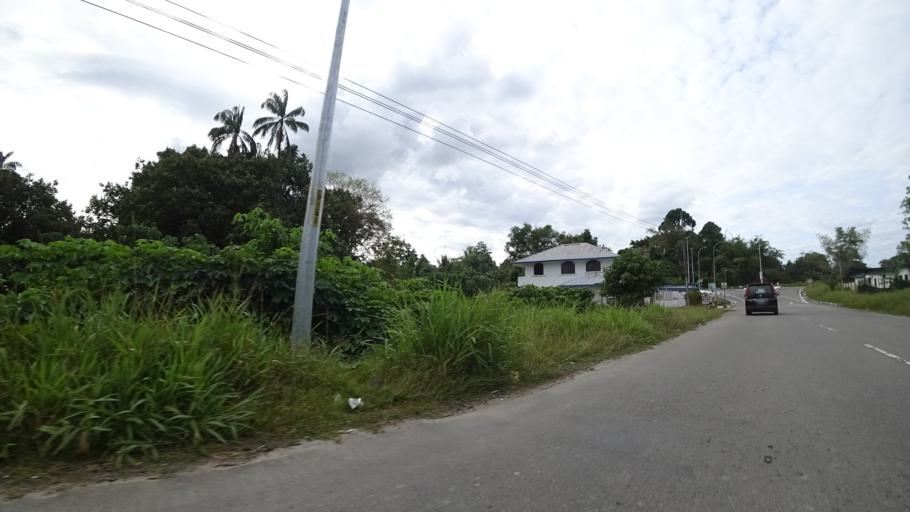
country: BN
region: Brunei and Muara
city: Bandar Seri Begawan
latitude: 4.8711
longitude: 114.9397
